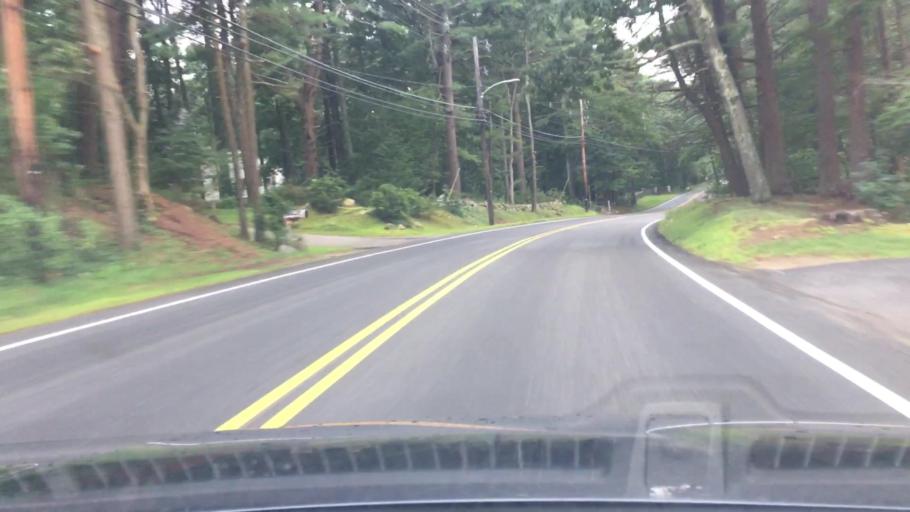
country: US
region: Massachusetts
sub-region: Essex County
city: Middleton
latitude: 42.5754
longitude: -71.0278
